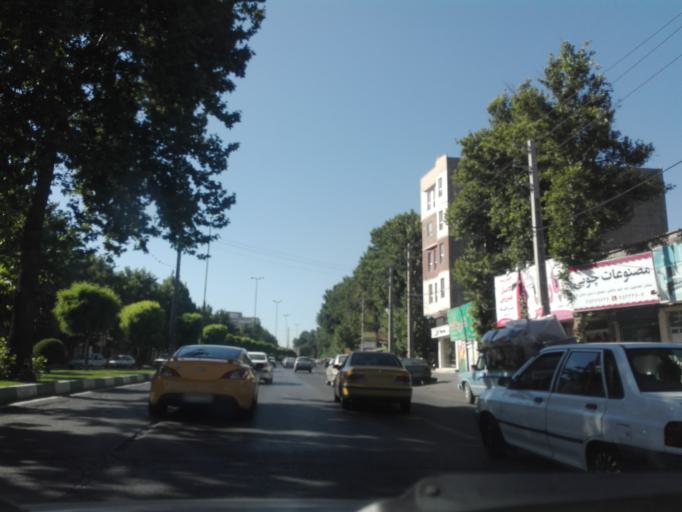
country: IR
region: Tehran
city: Shahriar
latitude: 35.6664
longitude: 51.0561
